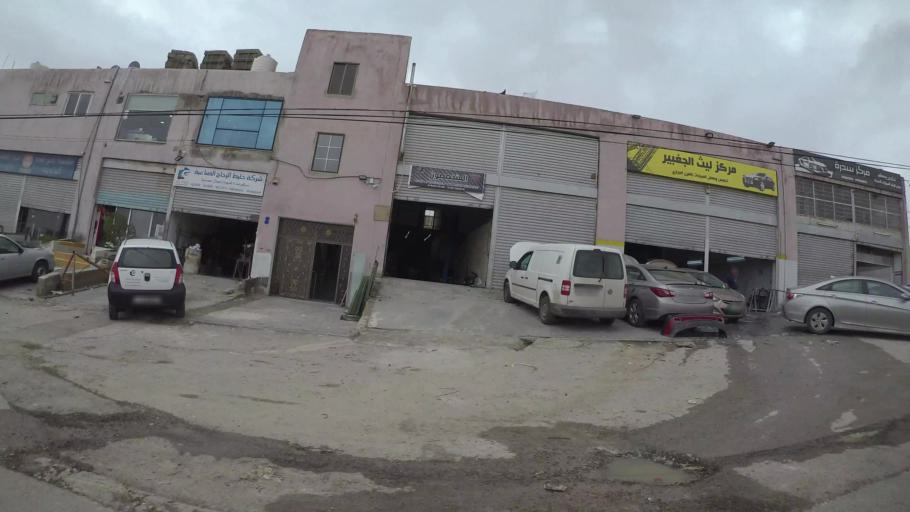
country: JO
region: Amman
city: Wadi as Sir
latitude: 31.9411
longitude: 35.8336
